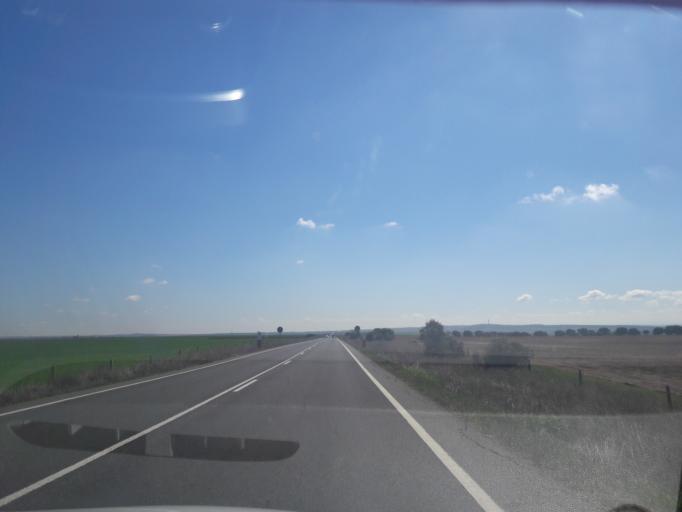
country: ES
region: Castille and Leon
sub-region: Provincia de Salamanca
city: Parada de Arriba
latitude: 40.9849
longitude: -5.8285
